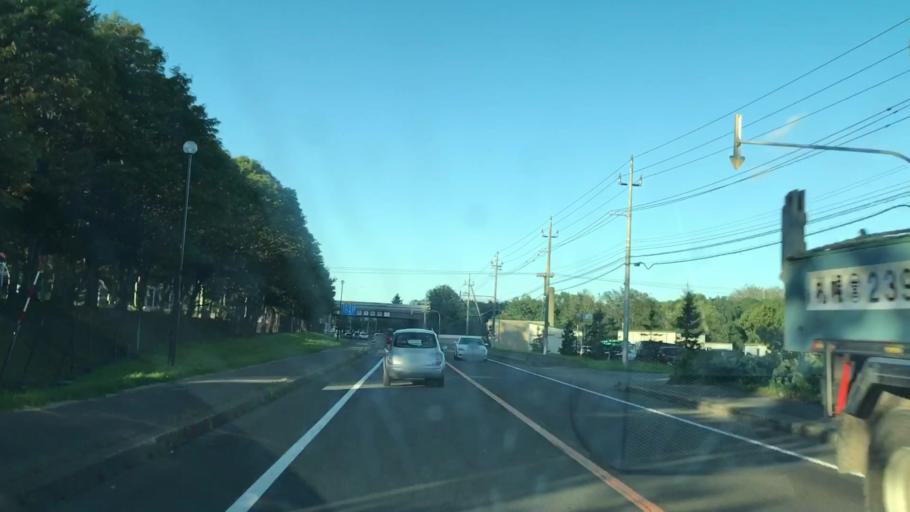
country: JP
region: Hokkaido
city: Niseko Town
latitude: 42.7474
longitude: 140.8989
